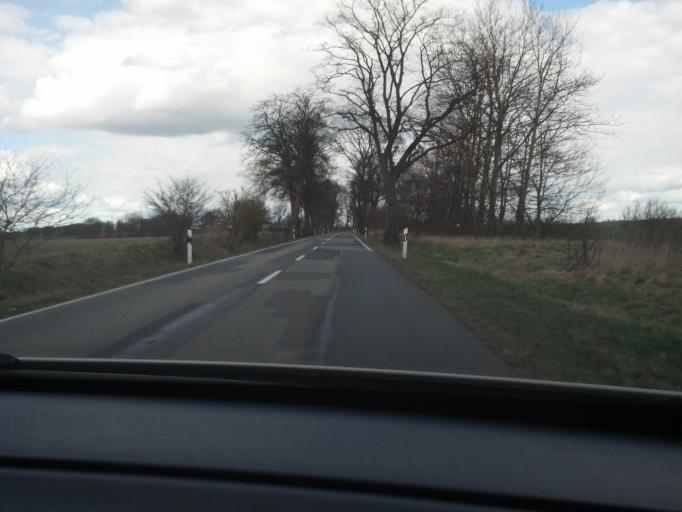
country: DE
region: Mecklenburg-Vorpommern
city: Loitz
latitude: 53.4261
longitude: 13.3544
